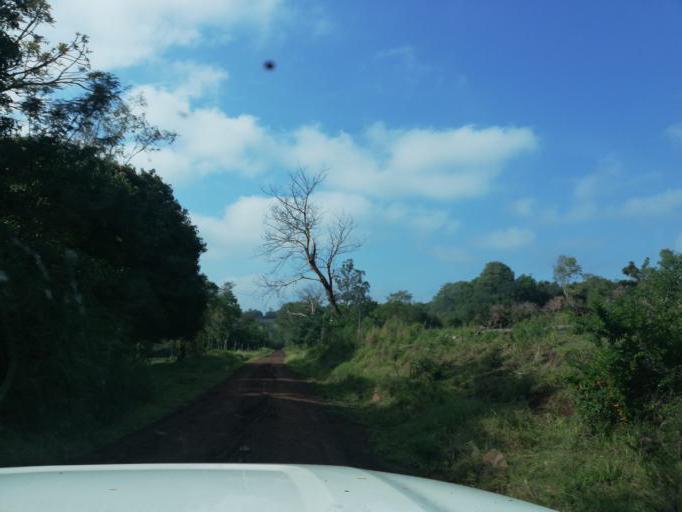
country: AR
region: Misiones
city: Cerro Azul
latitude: -27.6060
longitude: -55.5369
